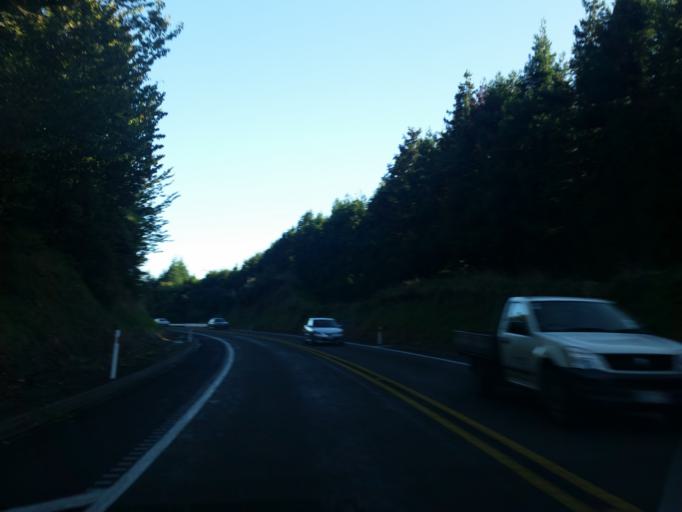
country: NZ
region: Bay of Plenty
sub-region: Western Bay of Plenty District
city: Katikati
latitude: -37.6482
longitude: 175.9943
